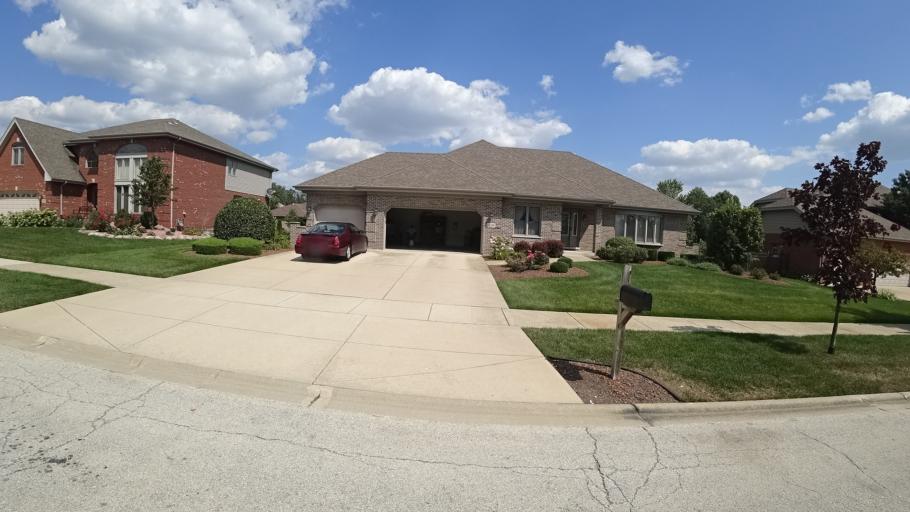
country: US
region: Illinois
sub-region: Cook County
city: Palos Heights
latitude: 41.6333
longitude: -87.8118
